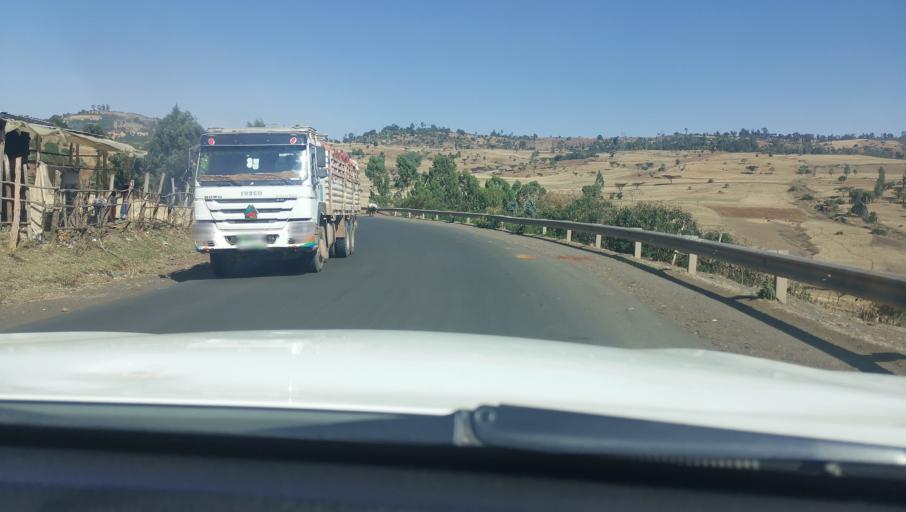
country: ET
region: Oromiya
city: Gedo
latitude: 8.9692
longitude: 37.5182
